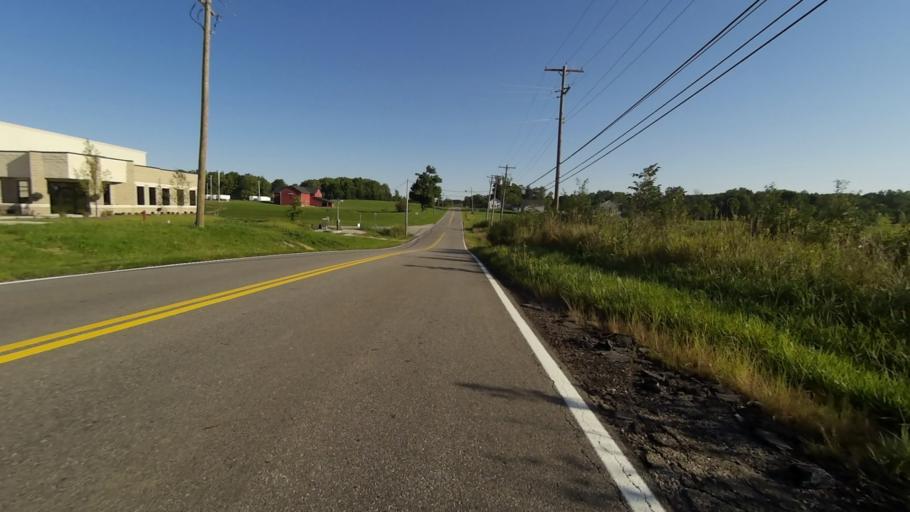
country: US
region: Ohio
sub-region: Portage County
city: Aurora
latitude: 41.2830
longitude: -81.3257
